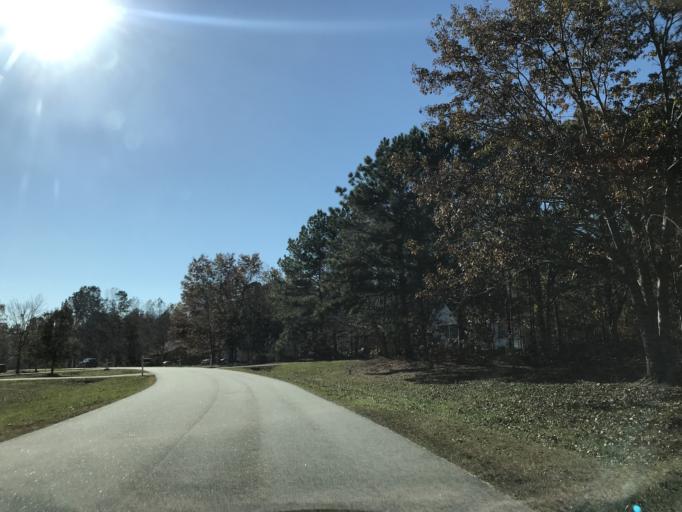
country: US
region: North Carolina
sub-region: Wake County
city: Rolesville
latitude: 35.9735
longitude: -78.3653
